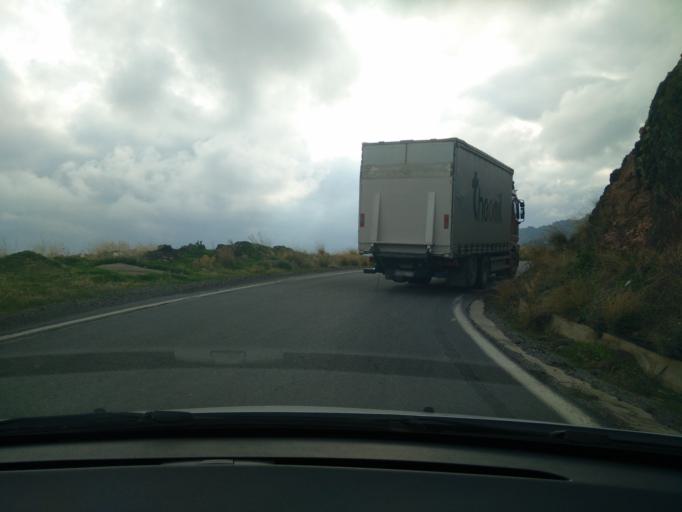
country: GR
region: Crete
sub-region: Nomos Lasithiou
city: Gra Liyia
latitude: 35.0223
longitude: 25.5587
